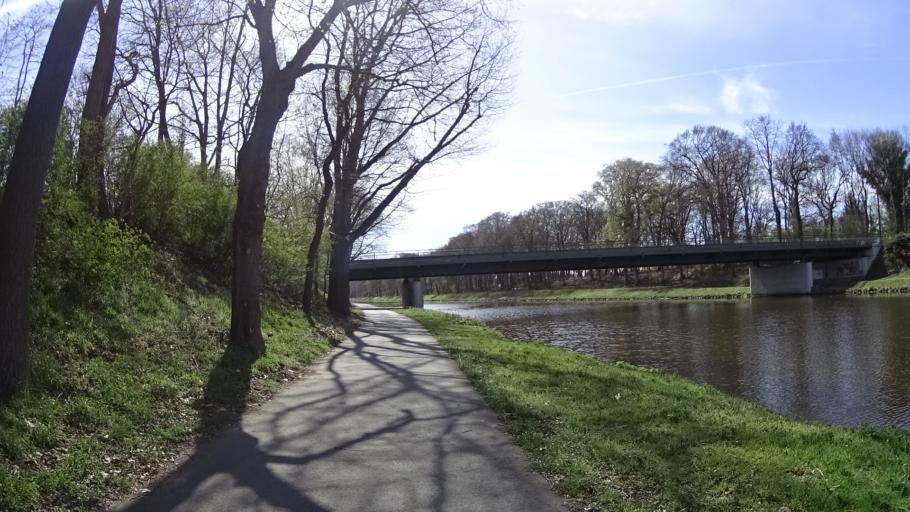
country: DE
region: Lower Saxony
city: Lingen
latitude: 52.5392
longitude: 7.2965
